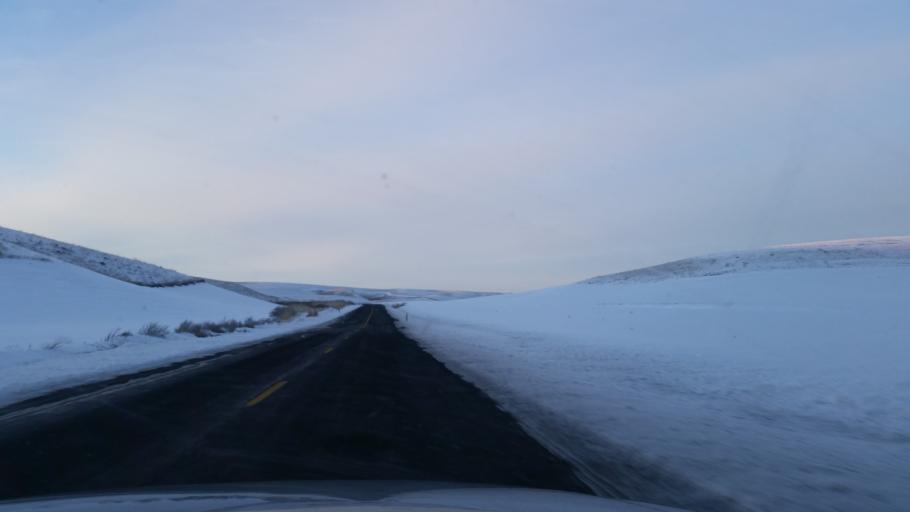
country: US
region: Washington
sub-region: Spokane County
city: Cheney
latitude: 47.1479
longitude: -117.8375
